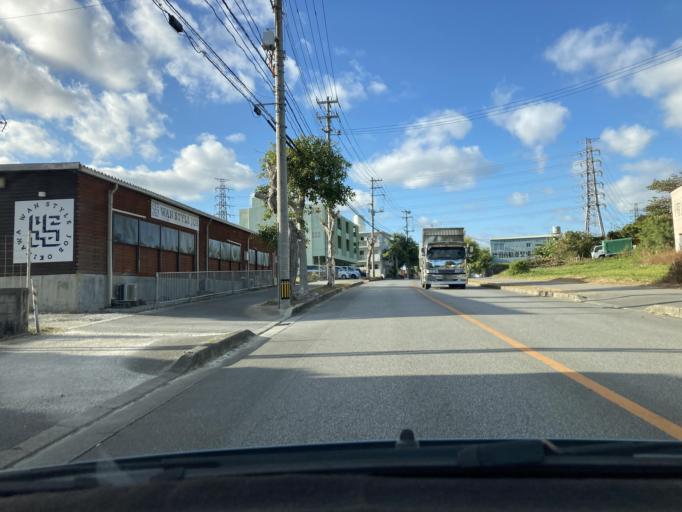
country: JP
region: Okinawa
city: Gushikawa
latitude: 26.3547
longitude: 127.8648
